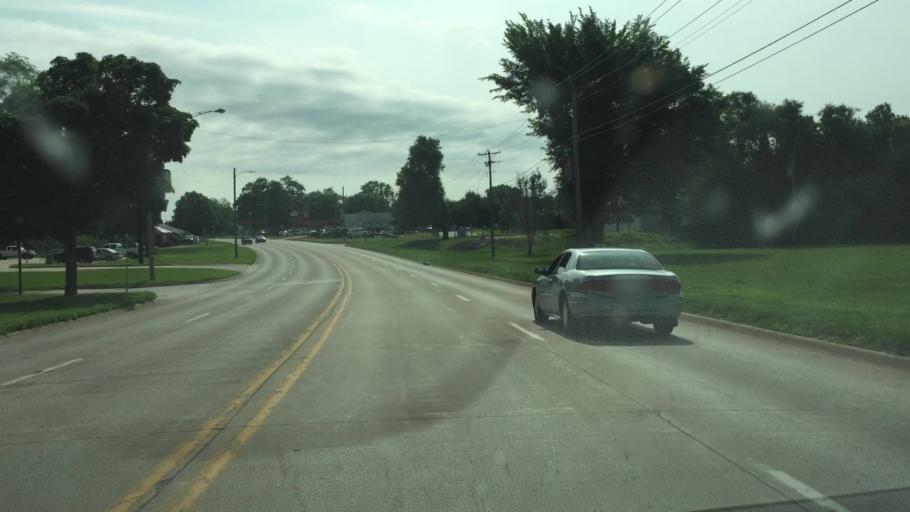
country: US
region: Iowa
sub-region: Lee County
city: Fort Madison
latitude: 40.6238
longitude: -91.3649
